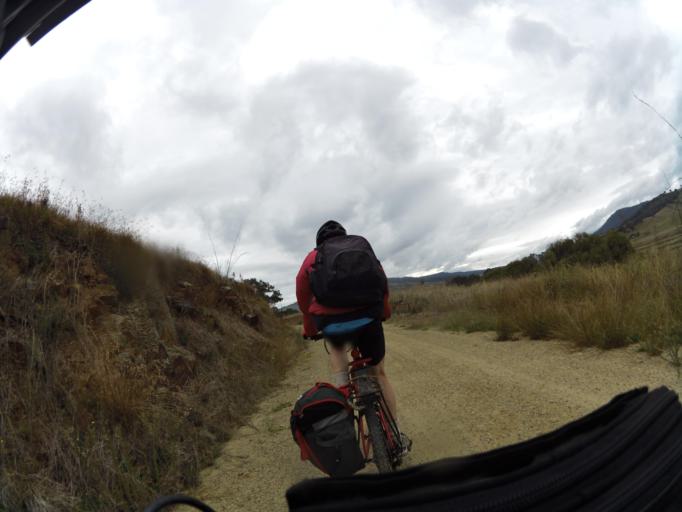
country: AU
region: New South Wales
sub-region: Albury Municipality
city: East Albury
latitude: -36.1919
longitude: 147.3003
